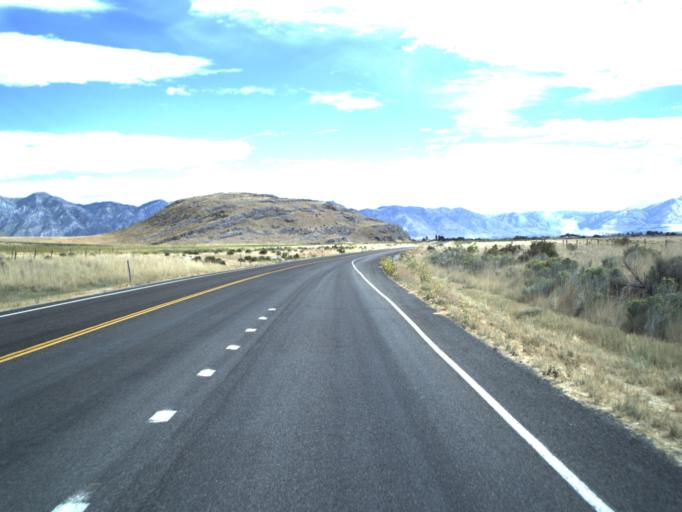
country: US
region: Utah
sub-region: Box Elder County
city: Elwood
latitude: 41.5788
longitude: -112.2461
